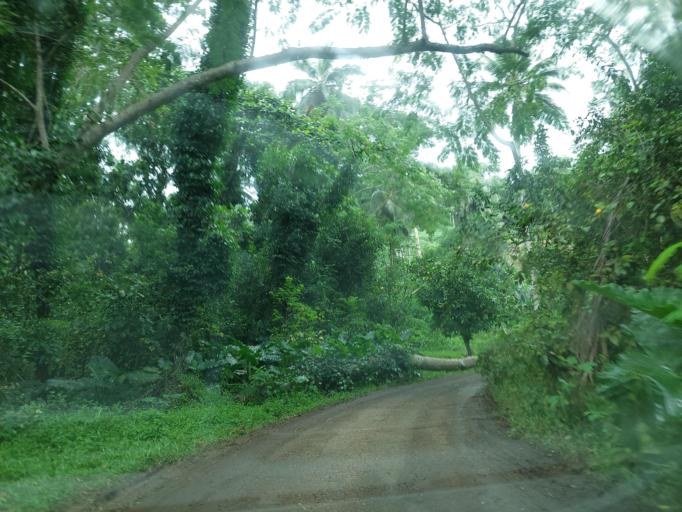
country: YT
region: Tsingoni
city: Tsingoni
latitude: -12.7660
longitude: 45.1164
